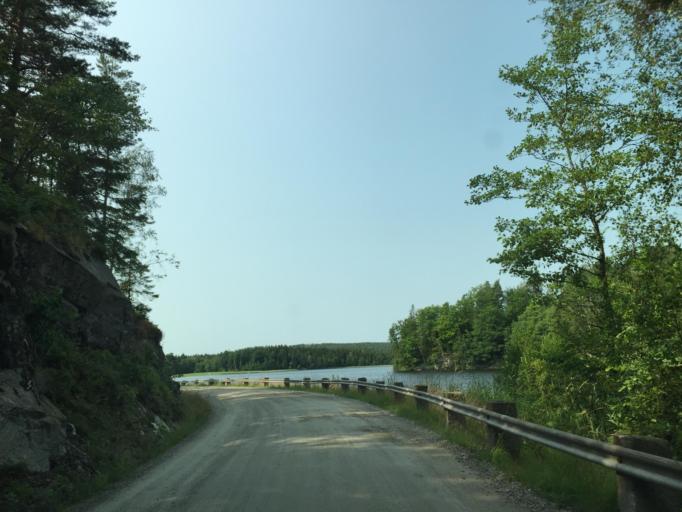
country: SE
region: Vaestra Goetaland
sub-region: Lilla Edets Kommun
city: Lilla Edet
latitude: 58.2360
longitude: 12.1102
